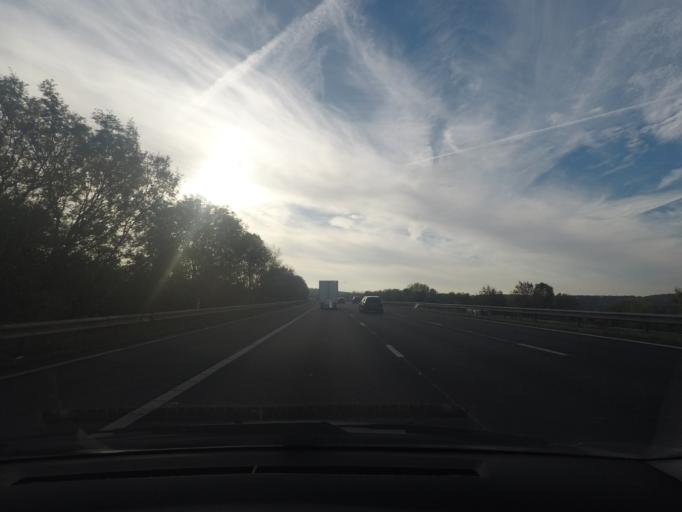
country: GB
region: England
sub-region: Barnsley
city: Darton
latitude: 53.5654
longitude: -1.5393
